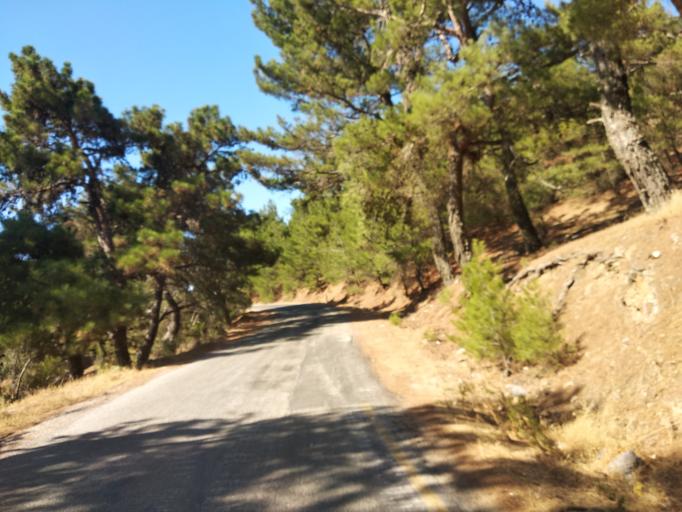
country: TR
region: Izmir
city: Gaziemir
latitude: 38.3021
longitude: 26.9978
